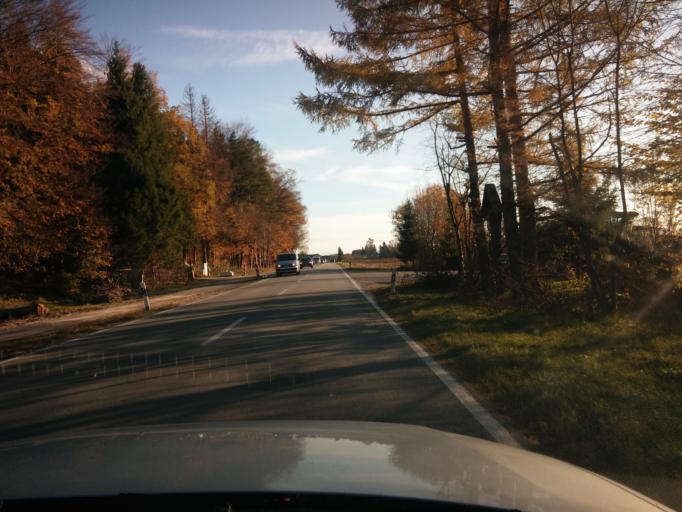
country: DE
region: Bavaria
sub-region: Upper Bavaria
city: Aying
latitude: 47.9576
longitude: 11.7840
